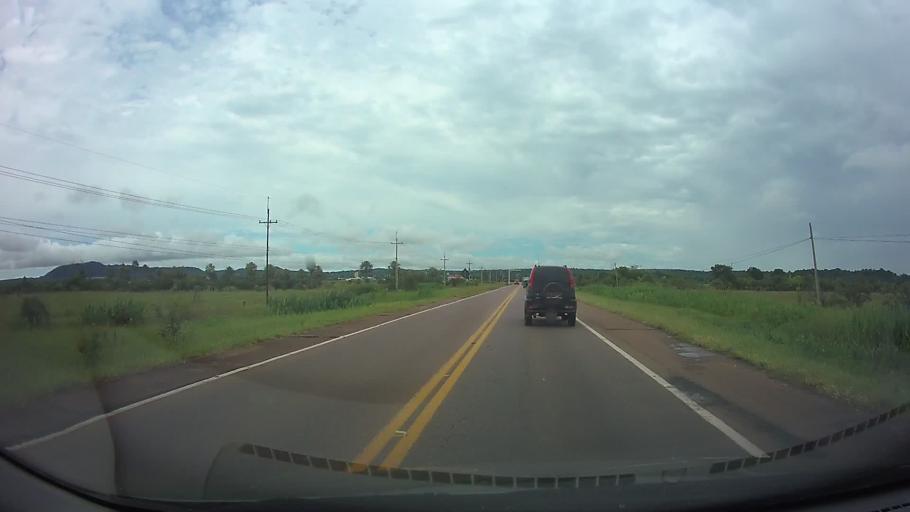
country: PY
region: Paraguari
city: Carapegua
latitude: -25.7508
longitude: -57.2202
